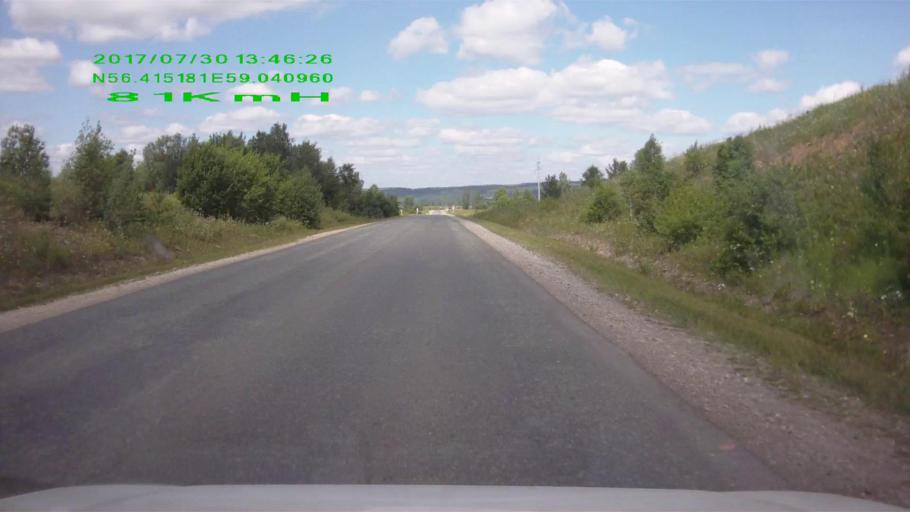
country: RU
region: Sverdlovsk
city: Mikhaylovsk
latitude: 56.4155
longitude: 59.0410
